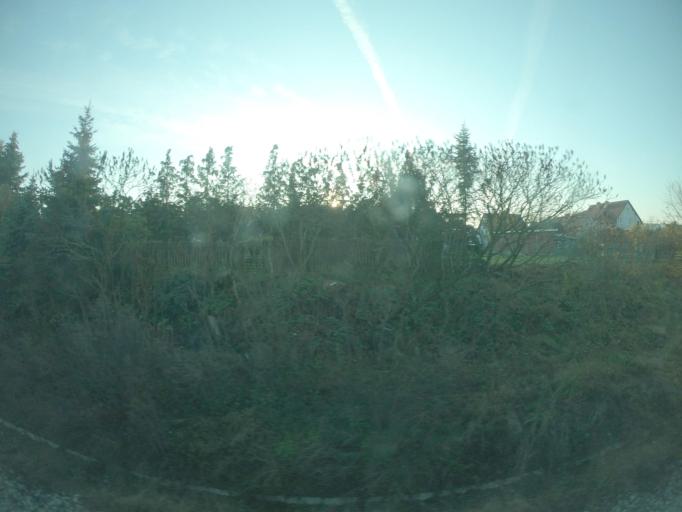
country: PL
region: Lubusz
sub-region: Powiat slubicki
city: Rzepin
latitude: 52.3481
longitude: 14.8232
